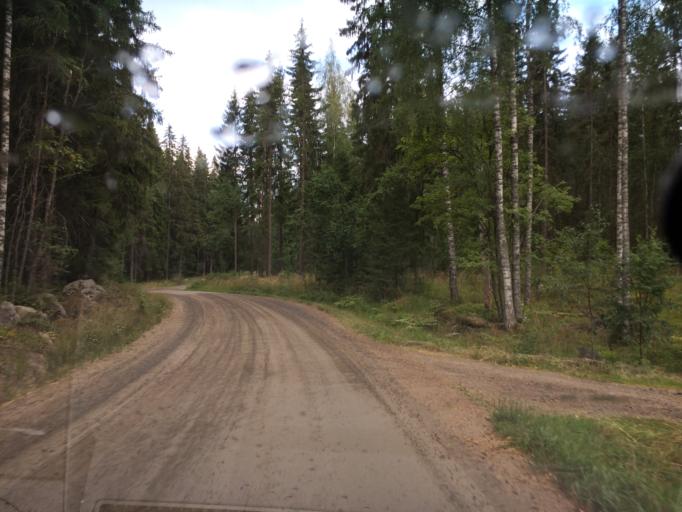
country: FI
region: Pirkanmaa
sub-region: Tampere
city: Luopioinen
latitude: 61.2736
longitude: 24.6712
